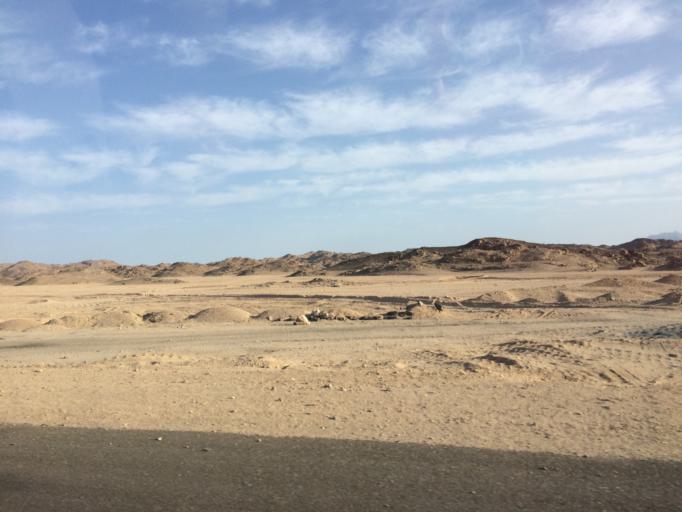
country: EG
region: Red Sea
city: Bur Safajah
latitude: 26.6564
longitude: 33.5486
